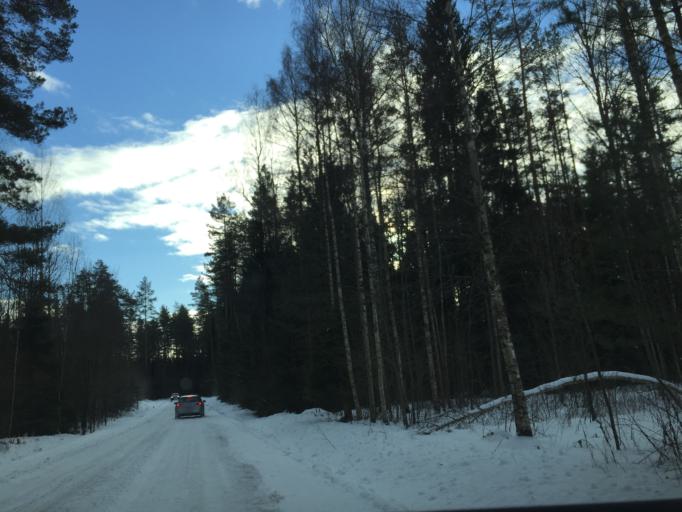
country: LV
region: Lielvarde
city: Lielvarde
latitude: 56.5646
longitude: 24.7979
